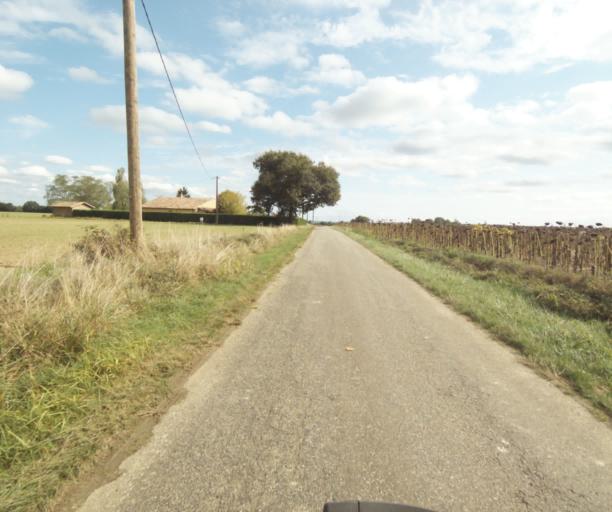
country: FR
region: Midi-Pyrenees
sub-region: Departement du Tarn-et-Garonne
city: Finhan
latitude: 43.8724
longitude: 1.1617
